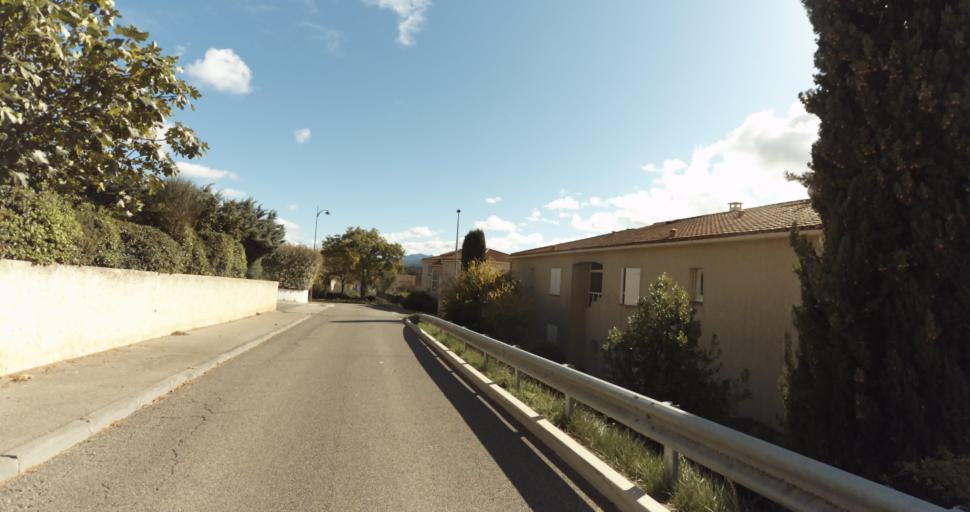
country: FR
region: Provence-Alpes-Cote d'Azur
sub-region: Departement des Bouches-du-Rhone
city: Venelles
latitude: 43.5982
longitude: 5.4798
